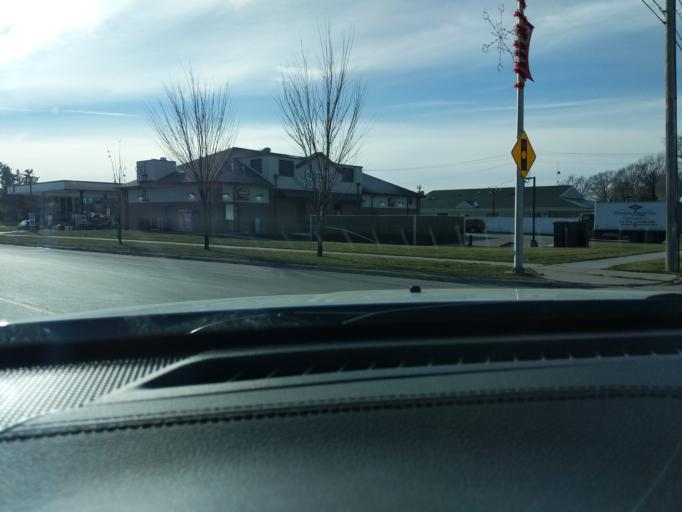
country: US
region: Minnesota
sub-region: Yellow Medicine County
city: Granite Falls
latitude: 44.8070
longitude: -95.5457
